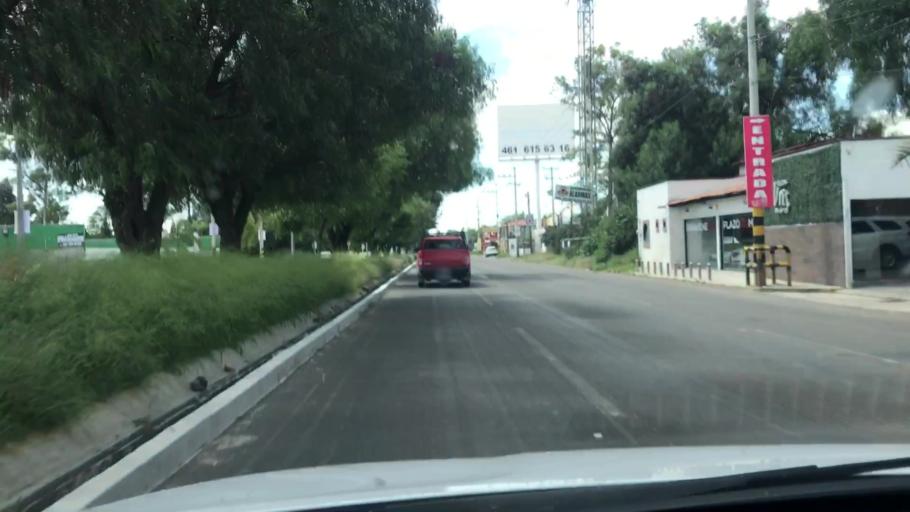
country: MX
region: Guanajuato
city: Celaya
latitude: 20.5247
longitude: -100.7781
